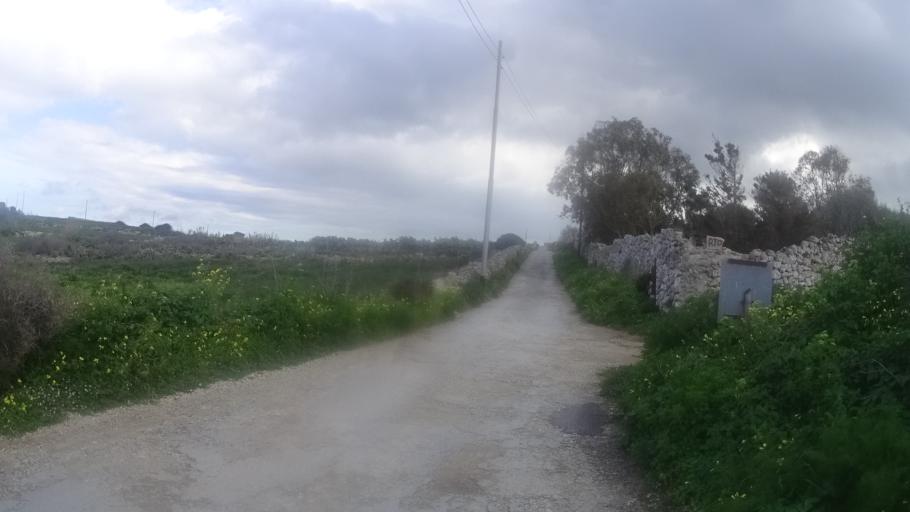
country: MT
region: L-Imgarr
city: Imgarr
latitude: 35.9021
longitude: 14.3691
